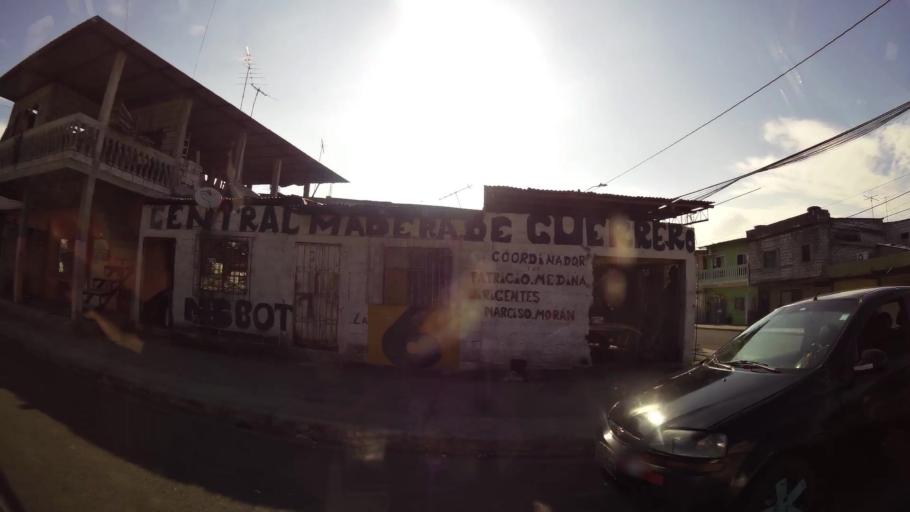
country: EC
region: Guayas
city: Guayaquil
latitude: -2.2238
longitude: -79.9310
